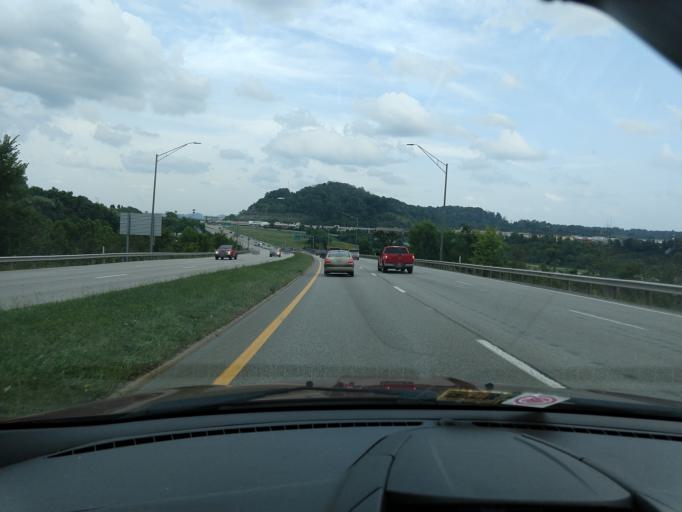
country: US
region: West Virginia
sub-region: Harrison County
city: Despard
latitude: 39.2777
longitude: -80.2894
